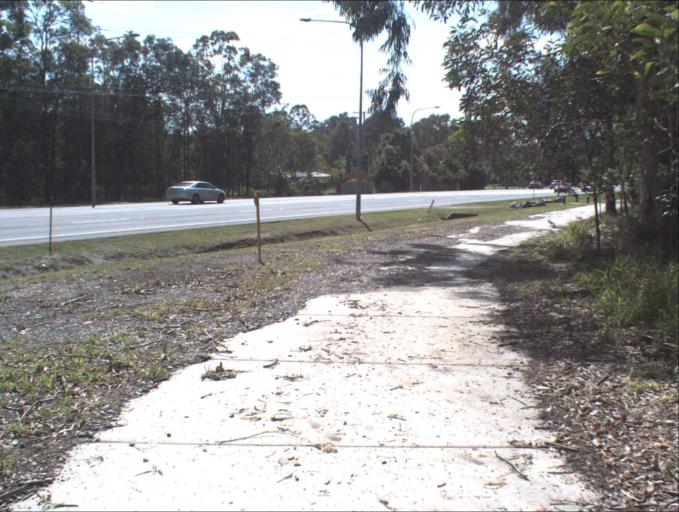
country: AU
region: Queensland
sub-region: Logan
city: Woodridge
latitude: -27.6556
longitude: 153.0669
